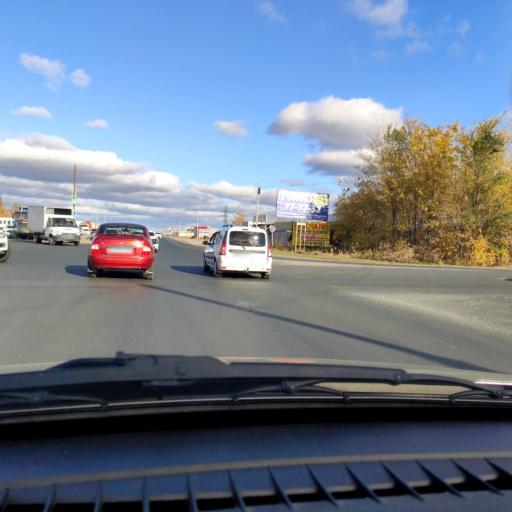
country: RU
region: Samara
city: Tol'yatti
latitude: 53.5602
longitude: 49.3582
